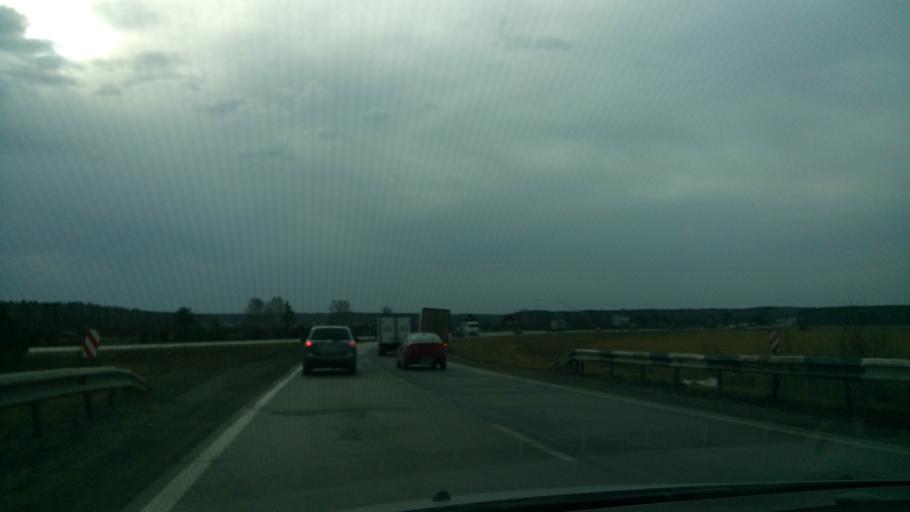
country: RU
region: Sverdlovsk
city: Verkhneye Dubrovo
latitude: 56.7377
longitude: 61.1022
